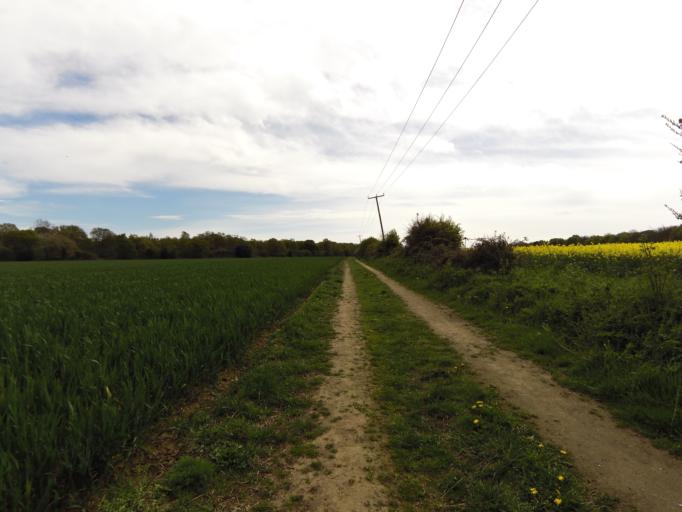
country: GB
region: England
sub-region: Suffolk
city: Ipswich
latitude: 52.0091
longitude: 1.1378
